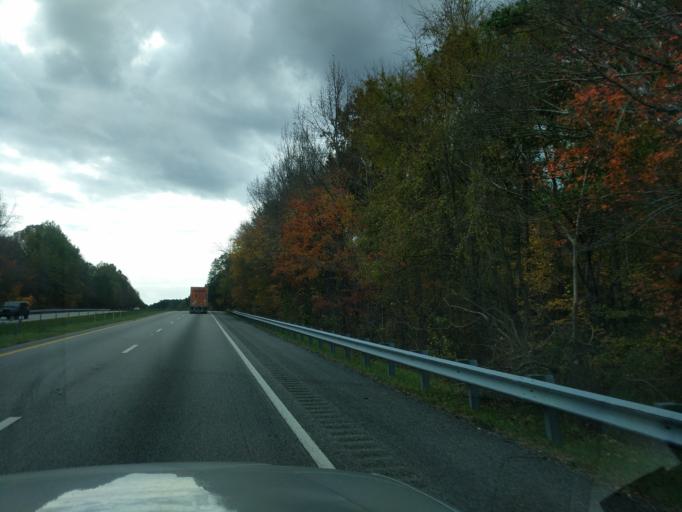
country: US
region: South Carolina
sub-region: Laurens County
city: Clinton
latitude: 34.5356
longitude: -81.8838
